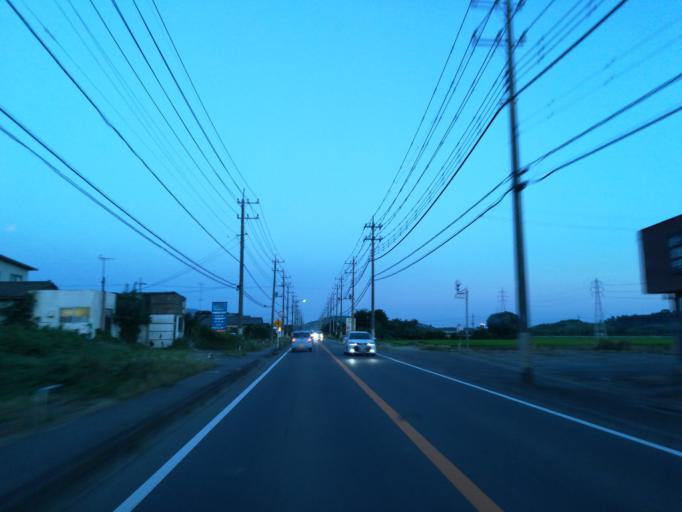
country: JP
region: Ibaraki
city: Tsukuba
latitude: 36.2133
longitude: 140.0693
